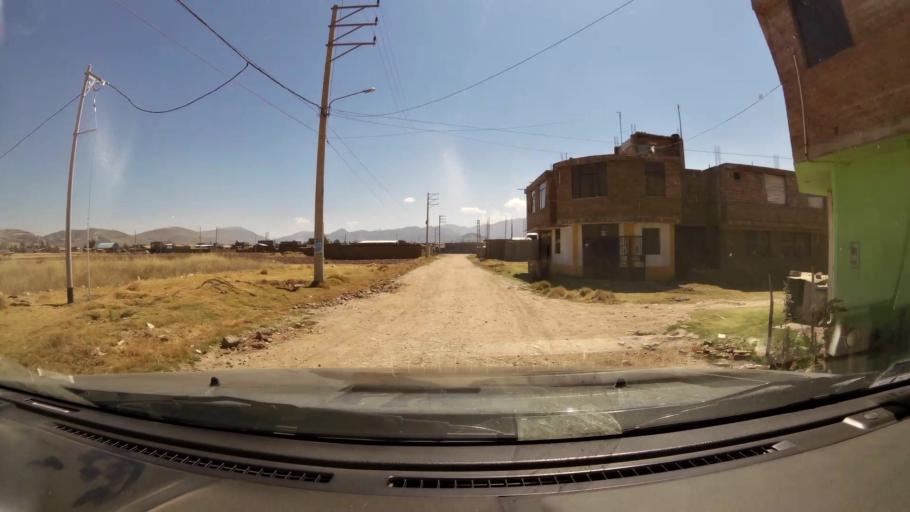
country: PE
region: Junin
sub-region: Provincia de Jauja
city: Sausa
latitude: -11.7809
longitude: -75.4852
